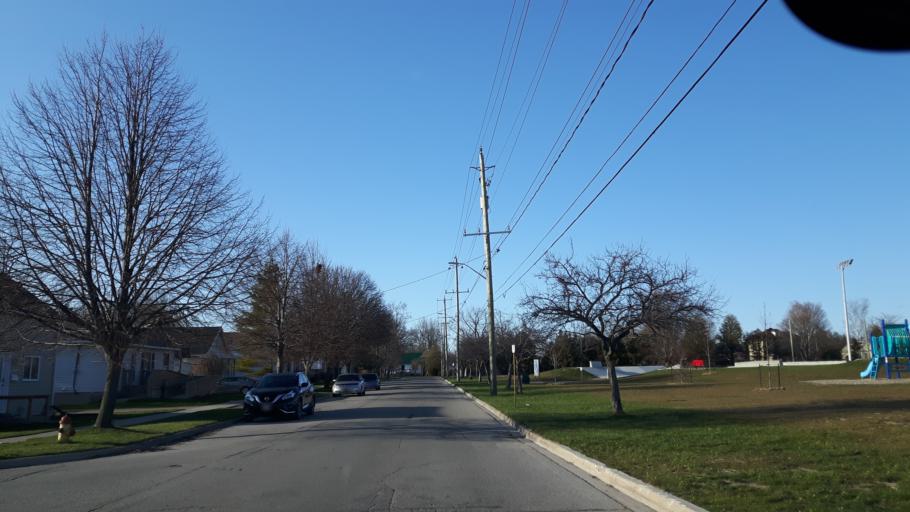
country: CA
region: Ontario
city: Goderich
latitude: 43.7373
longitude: -81.7164
